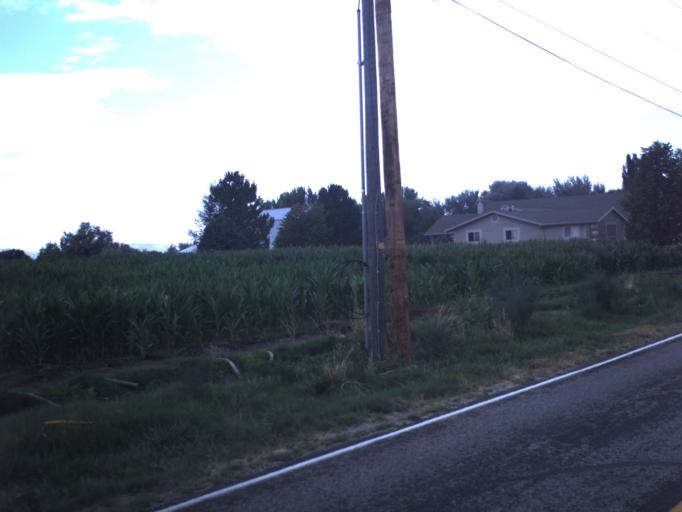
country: US
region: Utah
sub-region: Davis County
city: West Point
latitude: 41.1083
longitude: -112.1125
